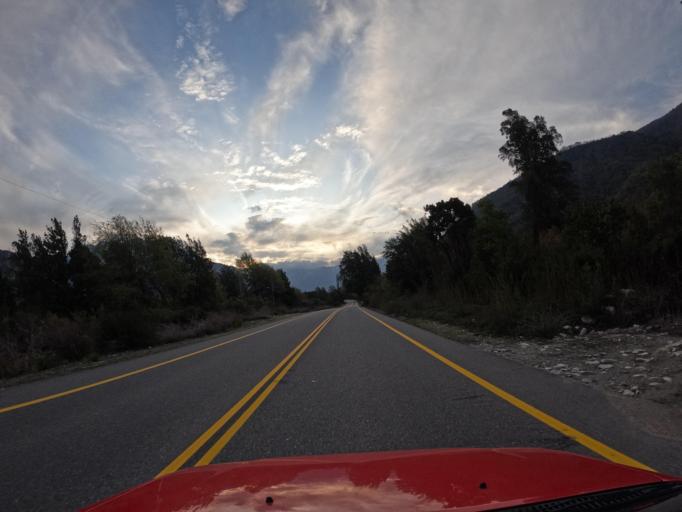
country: CL
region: Maule
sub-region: Provincia de Linares
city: Colbun
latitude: -35.7147
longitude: -71.0411
